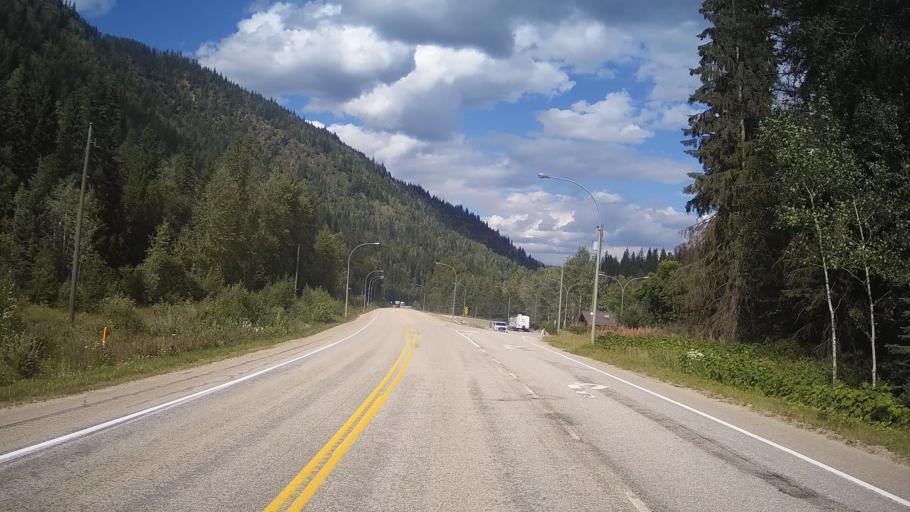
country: CA
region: British Columbia
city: Chase
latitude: 51.6841
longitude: -119.4225
